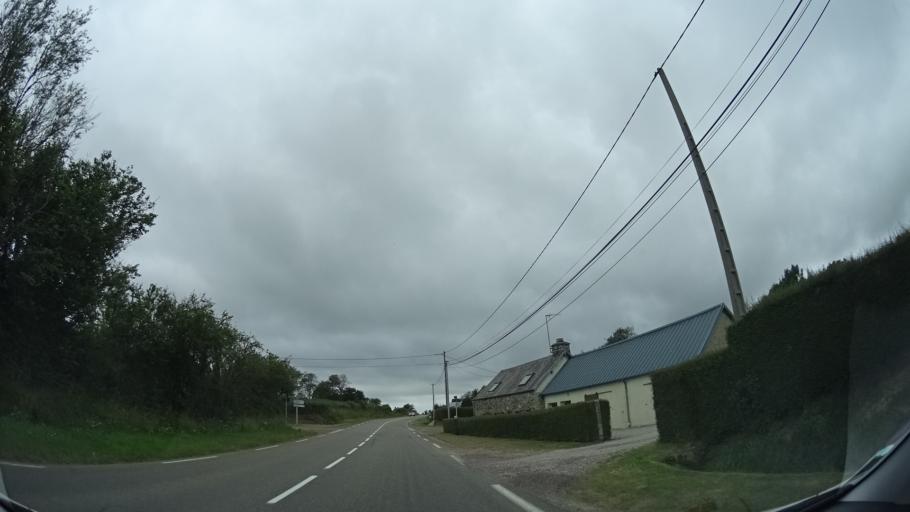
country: FR
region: Lower Normandy
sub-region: Departement de la Manche
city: La Haye-du-Puits
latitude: 49.3062
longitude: -1.5874
